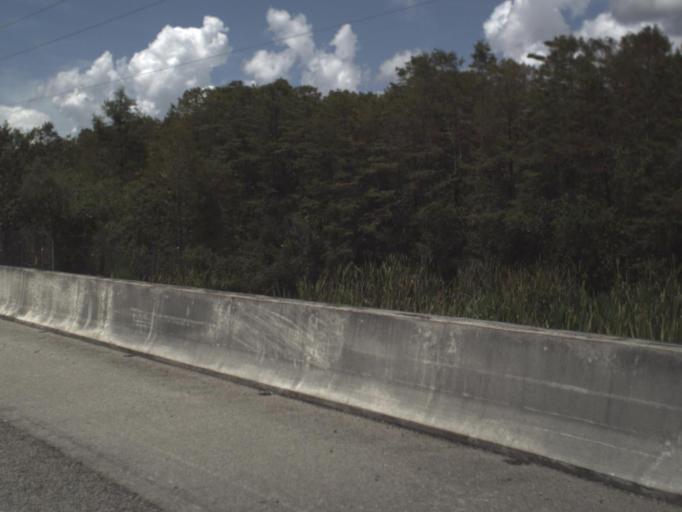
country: US
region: Florida
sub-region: Collier County
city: Immokalee
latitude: 26.1683
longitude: -81.1136
